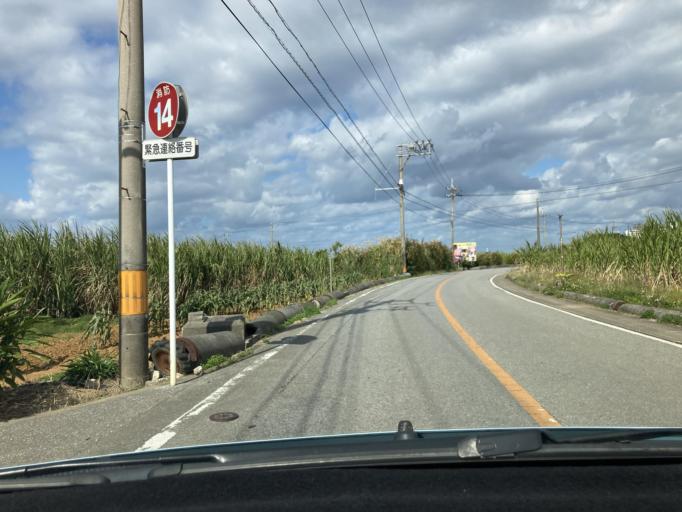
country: JP
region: Okinawa
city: Ishikawa
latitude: 26.4251
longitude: 127.7175
